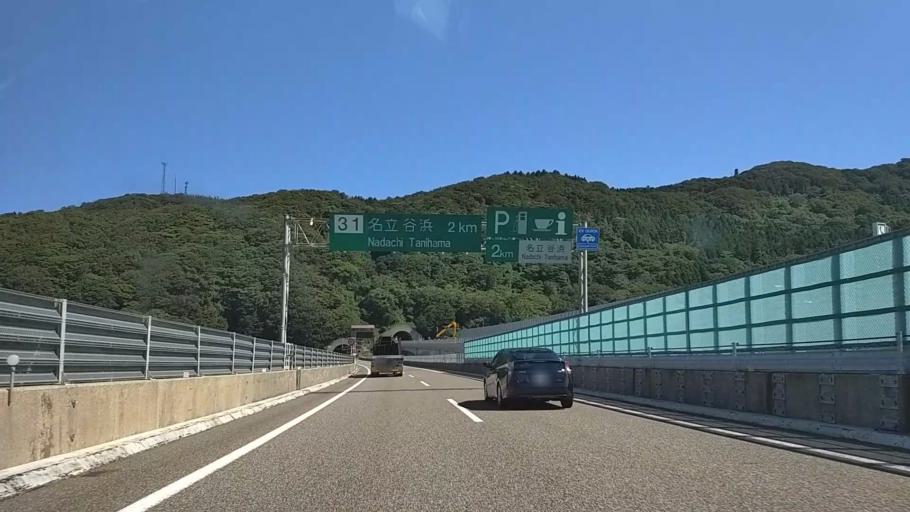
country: JP
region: Niigata
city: Joetsu
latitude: 37.1583
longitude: 138.0901
